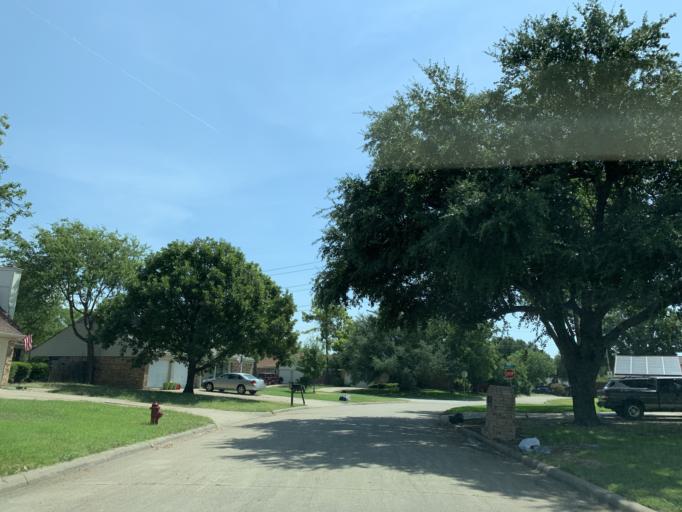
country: US
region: Texas
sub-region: Dallas County
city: Grand Prairie
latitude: 32.6653
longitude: -97.0386
